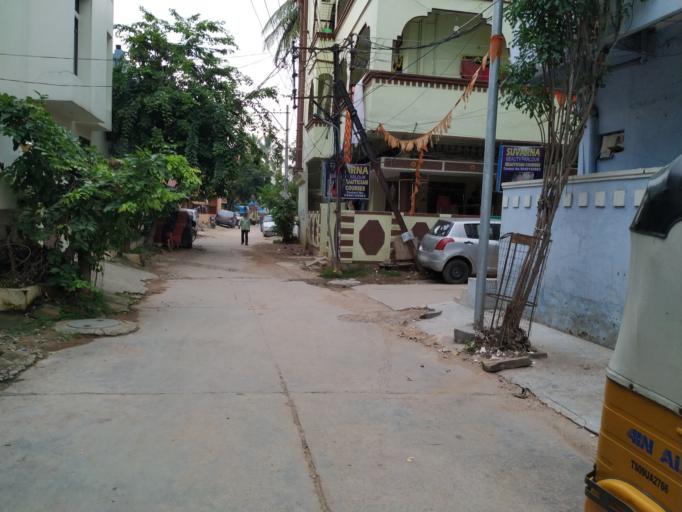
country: IN
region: Telangana
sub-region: Rangareddi
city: Quthbullapur
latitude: 17.4675
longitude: 78.4575
